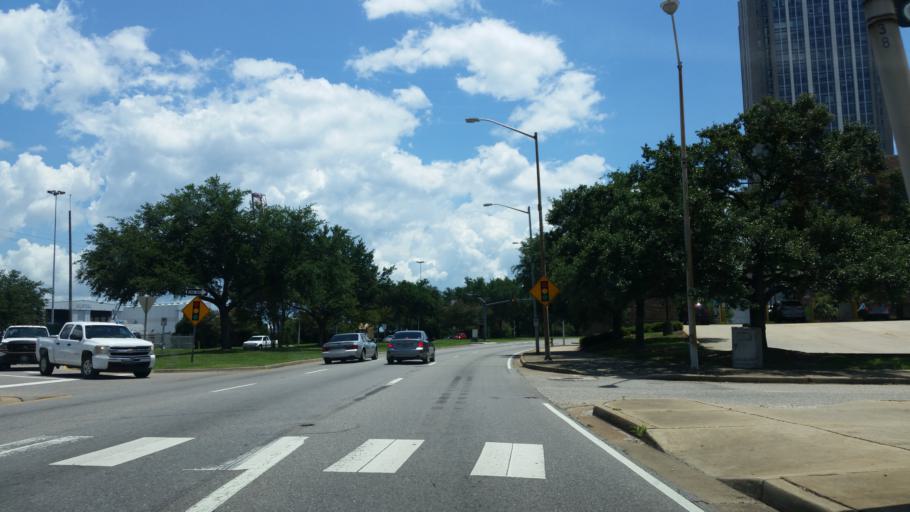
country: US
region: Alabama
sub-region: Mobile County
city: Mobile
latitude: 30.6962
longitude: -88.0404
